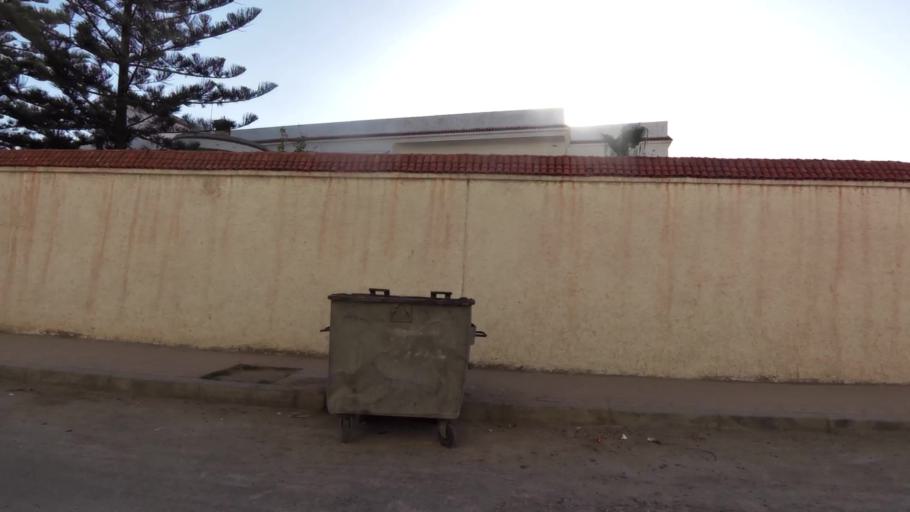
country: MA
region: Tanger-Tetouan
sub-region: Tetouan
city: Martil
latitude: 35.6167
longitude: -5.2814
